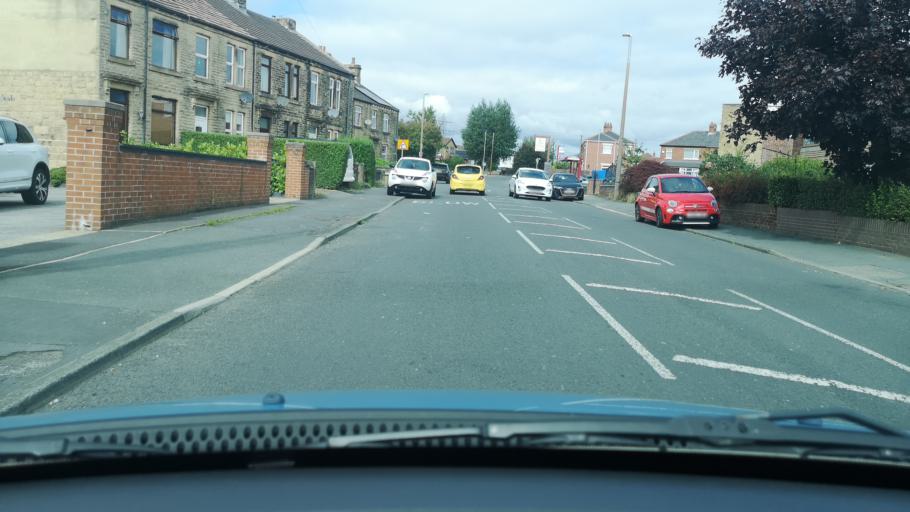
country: GB
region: England
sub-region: Kirklees
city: Liversedge
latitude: 53.6905
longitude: -1.6963
